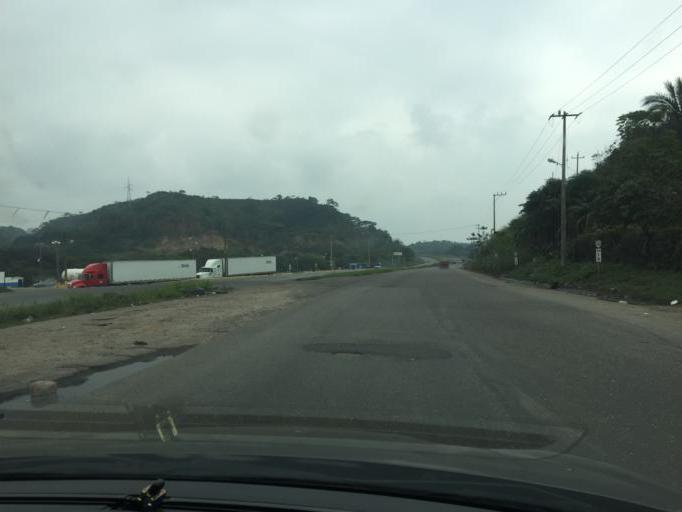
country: MX
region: Veracruz
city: Villa Nanchital
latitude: 18.0723
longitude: -94.3147
